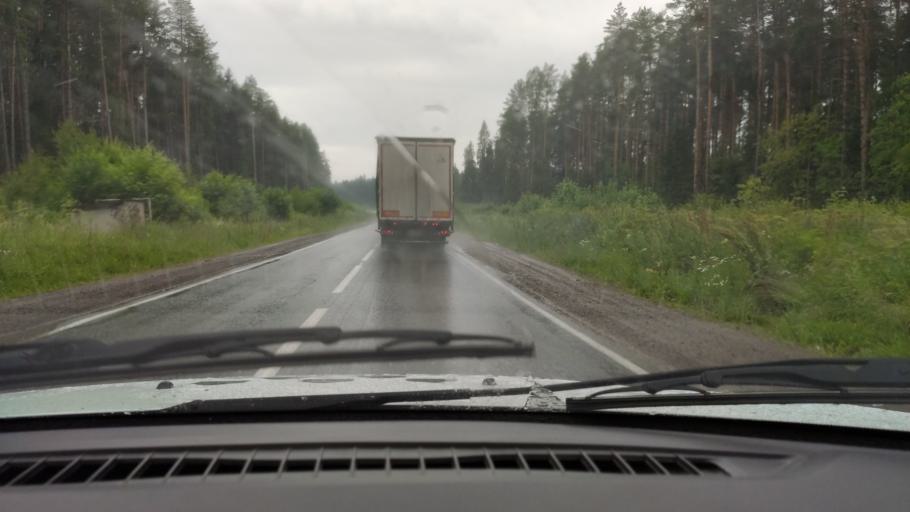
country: RU
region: Udmurtiya
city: Votkinsk
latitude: 57.0861
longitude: 54.0558
